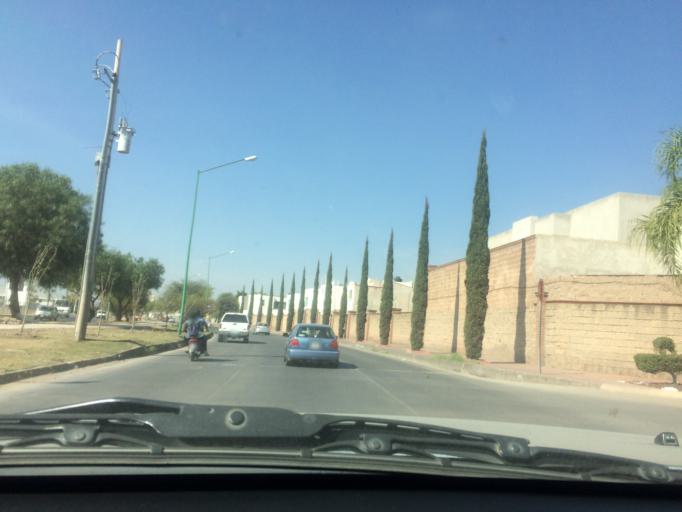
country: MX
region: Guanajuato
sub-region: Leon
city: Medina
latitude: 21.1249
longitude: -101.6210
